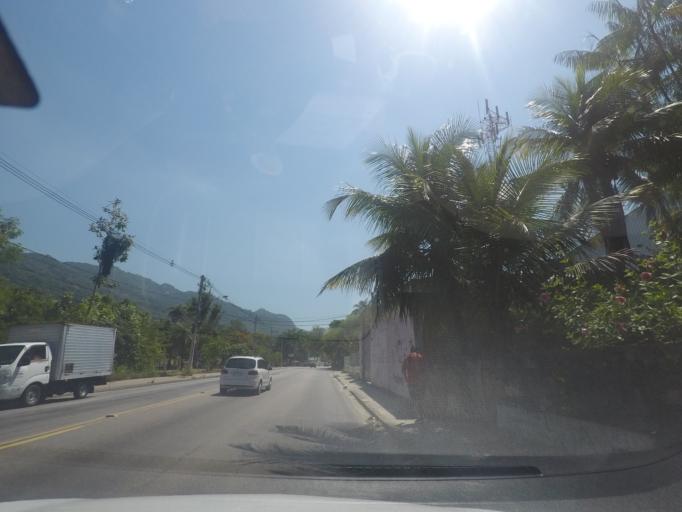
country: BR
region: Rio de Janeiro
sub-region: Nilopolis
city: Nilopolis
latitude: -22.9833
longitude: -43.4699
